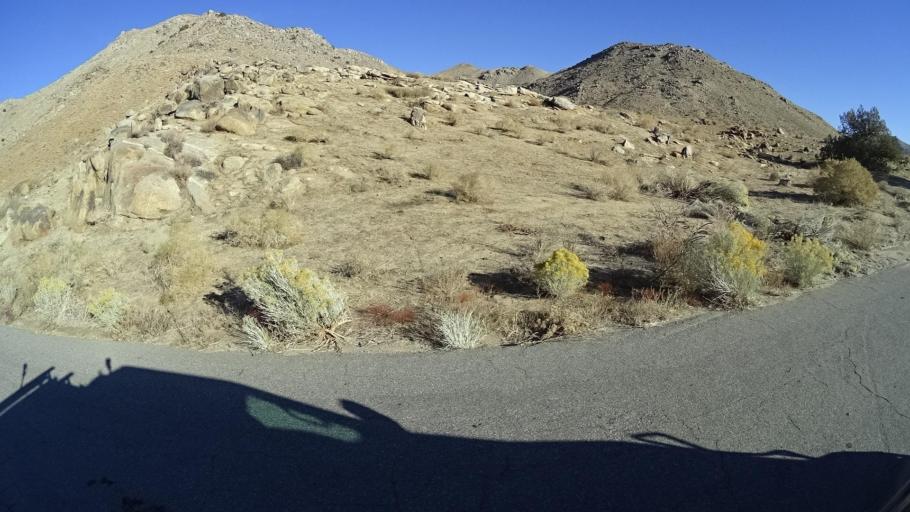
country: US
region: California
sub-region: Kern County
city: Weldon
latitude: 35.5714
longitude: -118.2508
